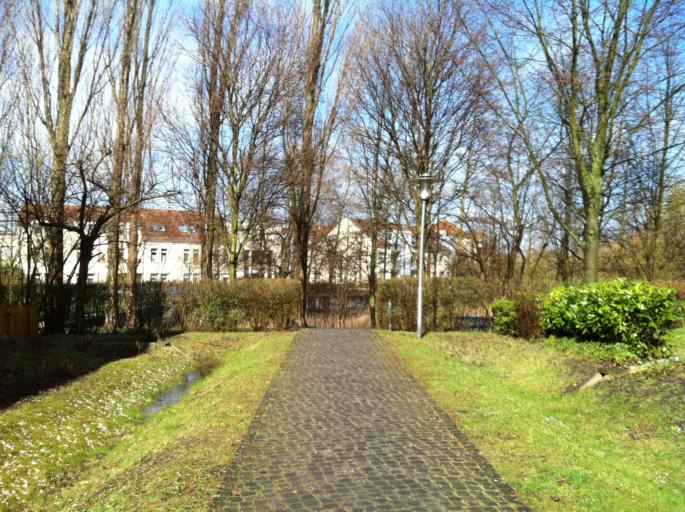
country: DE
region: Berlin
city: Karow
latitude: 52.6206
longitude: 13.4836
